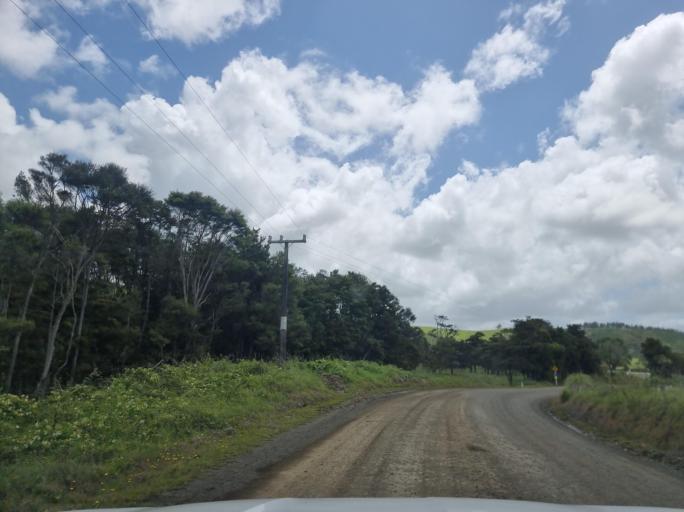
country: NZ
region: Northland
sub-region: Kaipara District
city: Dargaville
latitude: -36.1136
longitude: 174.1319
